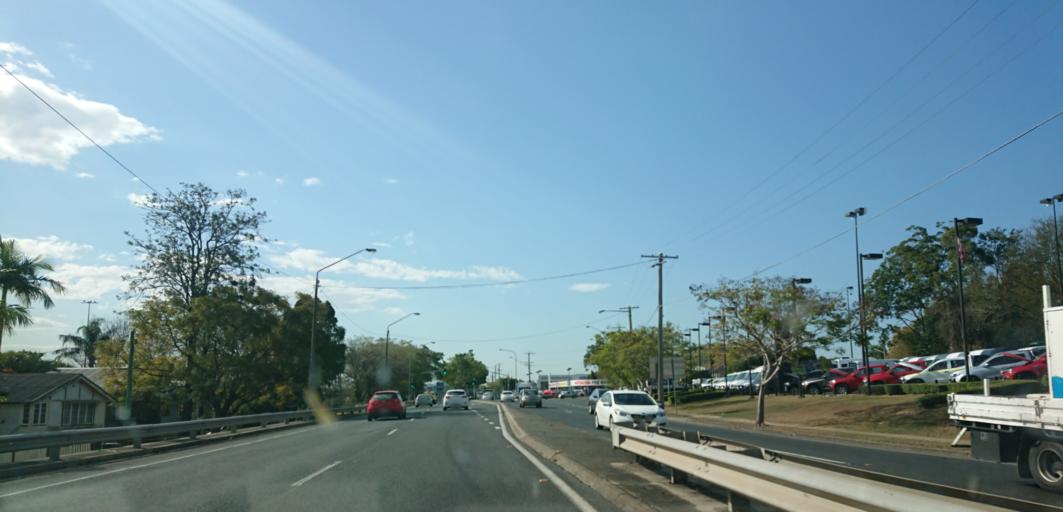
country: AU
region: Queensland
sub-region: Brisbane
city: Rocklea
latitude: -27.5395
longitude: 153.0134
